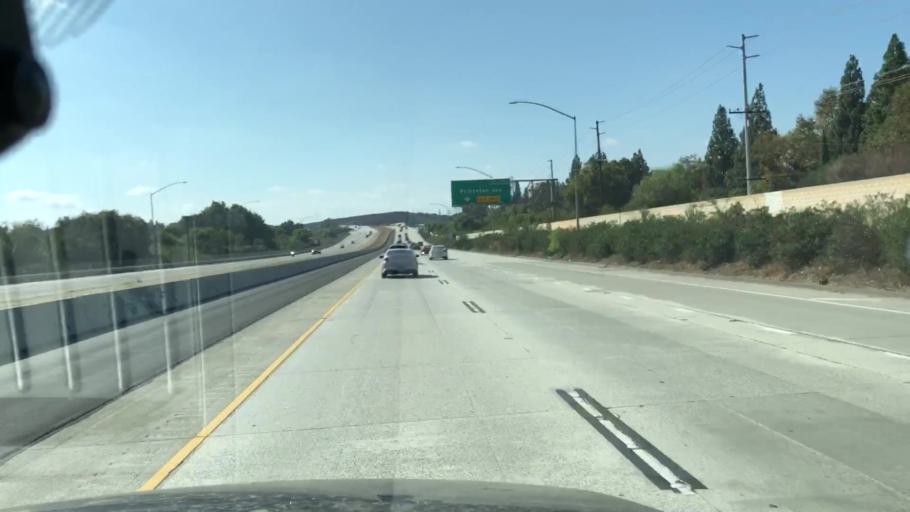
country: US
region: California
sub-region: Ventura County
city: Moorpark
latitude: 34.2934
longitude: -118.8462
